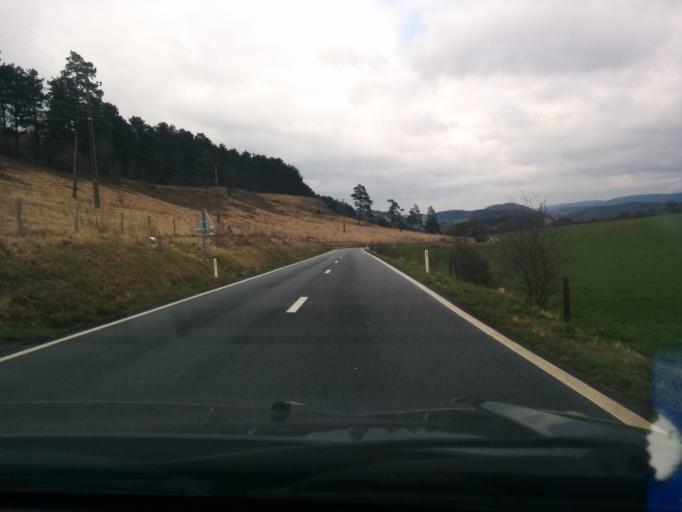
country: FR
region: Champagne-Ardenne
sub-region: Departement des Ardennes
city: Vireux-Molhain
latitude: 50.0874
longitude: 4.6438
